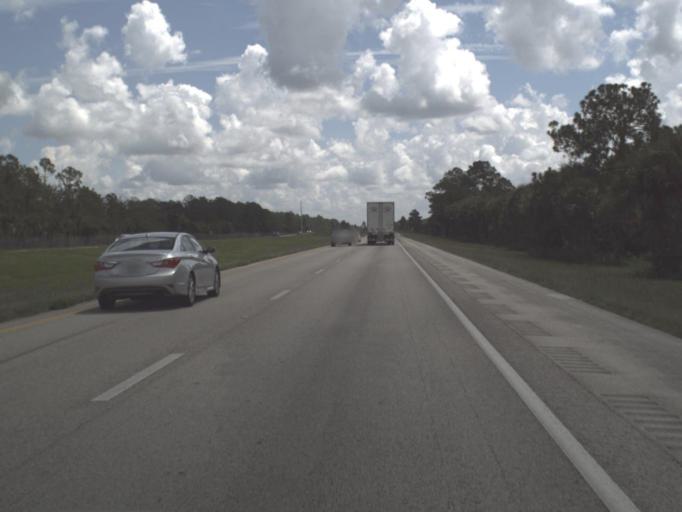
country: US
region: Florida
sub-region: Collier County
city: Orangetree
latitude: 26.1530
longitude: -81.4729
